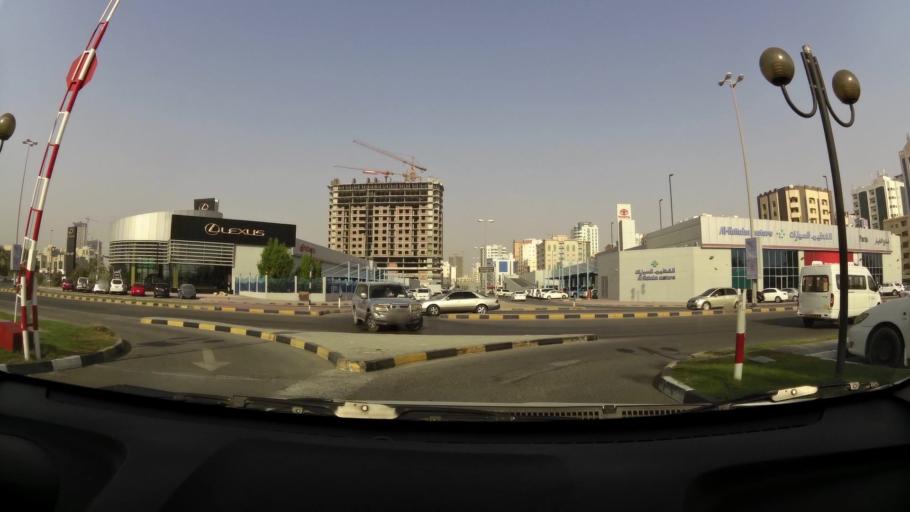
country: AE
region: Ajman
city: Ajman
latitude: 25.3901
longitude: 55.4458
